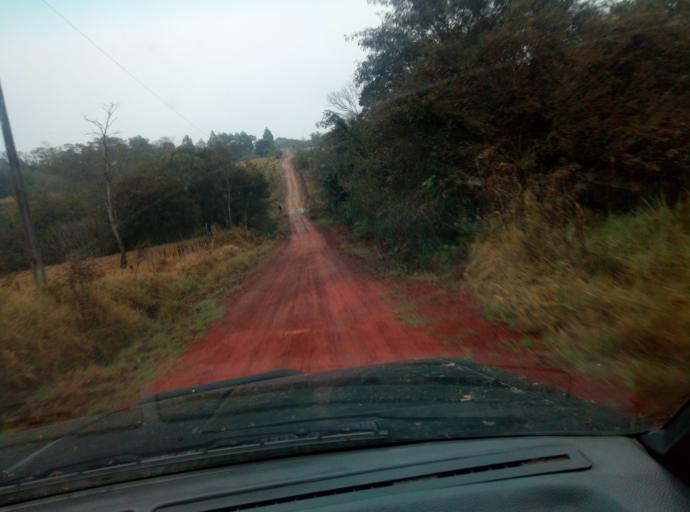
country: PY
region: Caaguazu
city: Carayao
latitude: -25.1904
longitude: -56.3143
